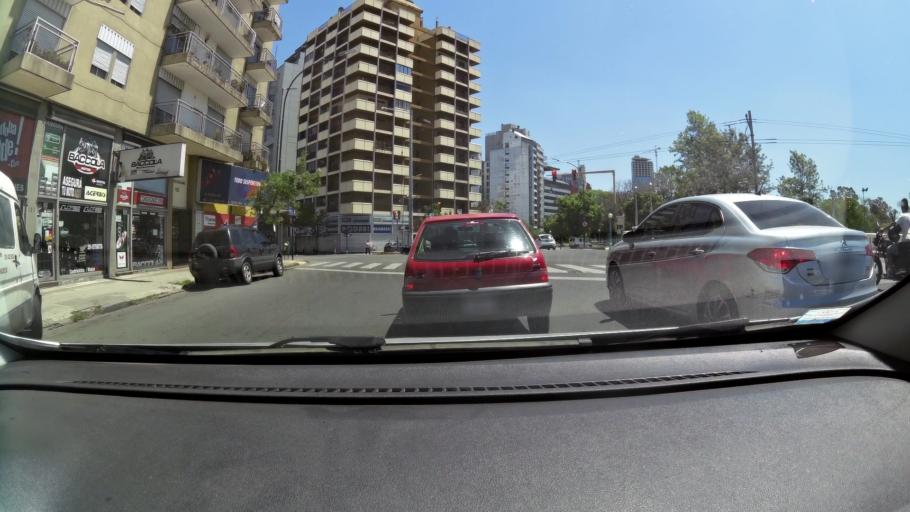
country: AR
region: Cordoba
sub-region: Departamento de Capital
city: Cordoba
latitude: -31.4070
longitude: -64.1831
